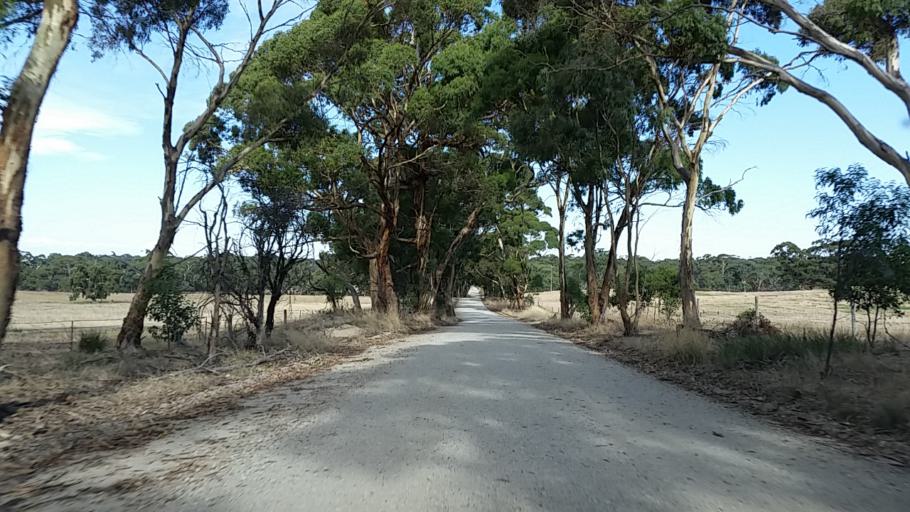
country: AU
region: South Australia
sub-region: Barossa
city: Angaston
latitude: -34.5729
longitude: 139.1202
